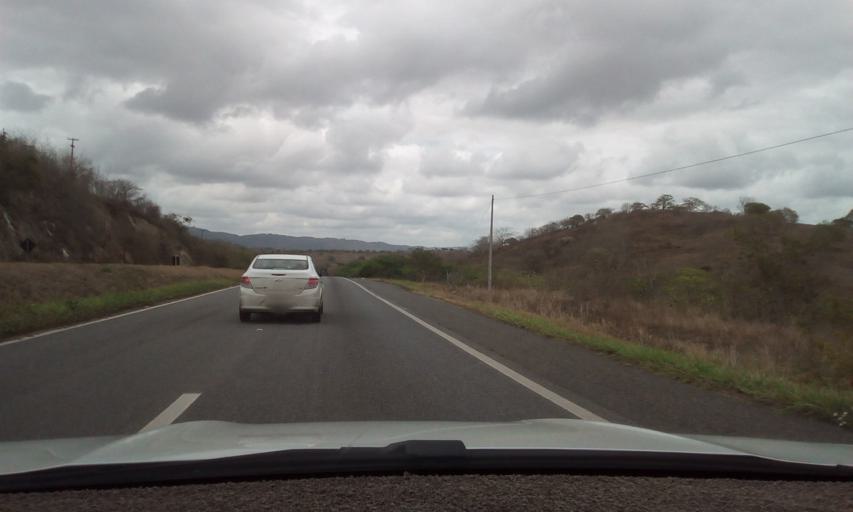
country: BR
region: Paraiba
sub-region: Massaranduba
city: Massaranduba
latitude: -7.2738
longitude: -35.7537
